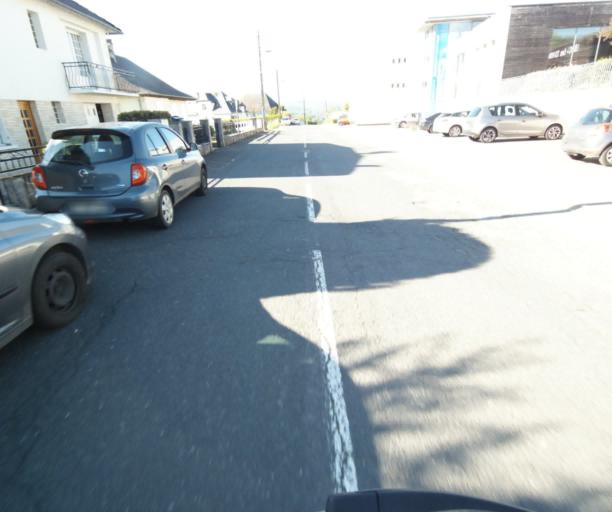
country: FR
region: Limousin
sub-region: Departement de la Correze
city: Tulle
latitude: 45.2681
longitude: 1.7858
